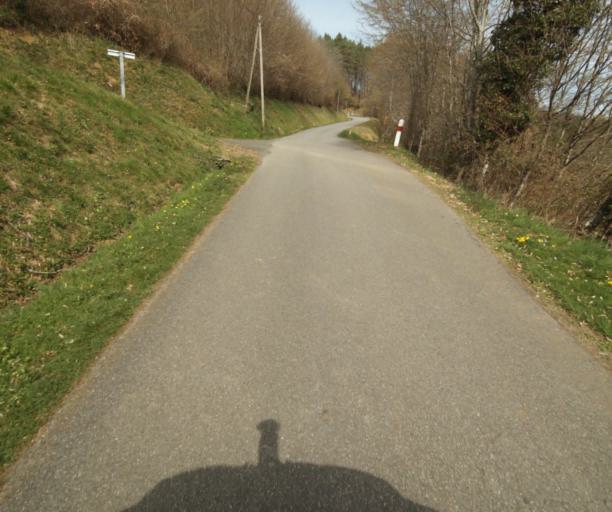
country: FR
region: Limousin
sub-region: Departement de la Correze
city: Naves
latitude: 45.3244
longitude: 1.8065
